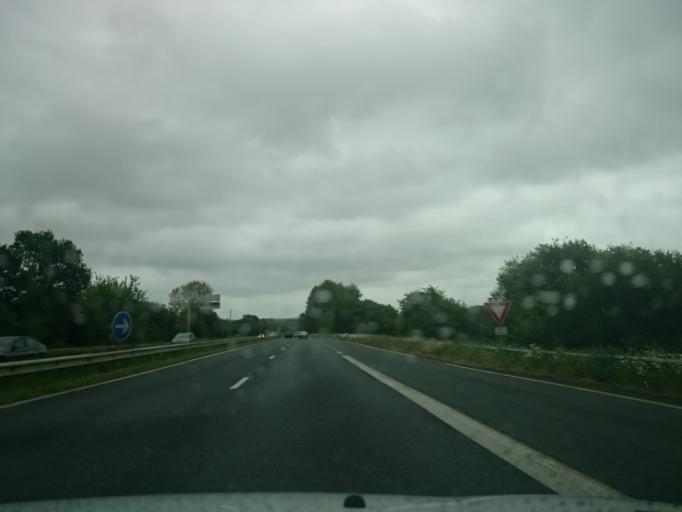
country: FR
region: Brittany
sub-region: Departement des Cotes-d'Armor
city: Plouagat
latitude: 48.5324
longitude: -3.0061
